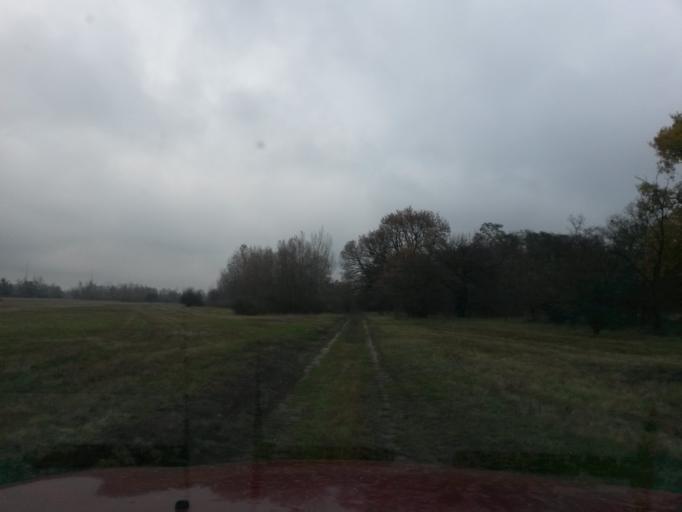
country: SK
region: Kosicky
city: Cierna nad Tisou
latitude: 48.5234
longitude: 21.9533
